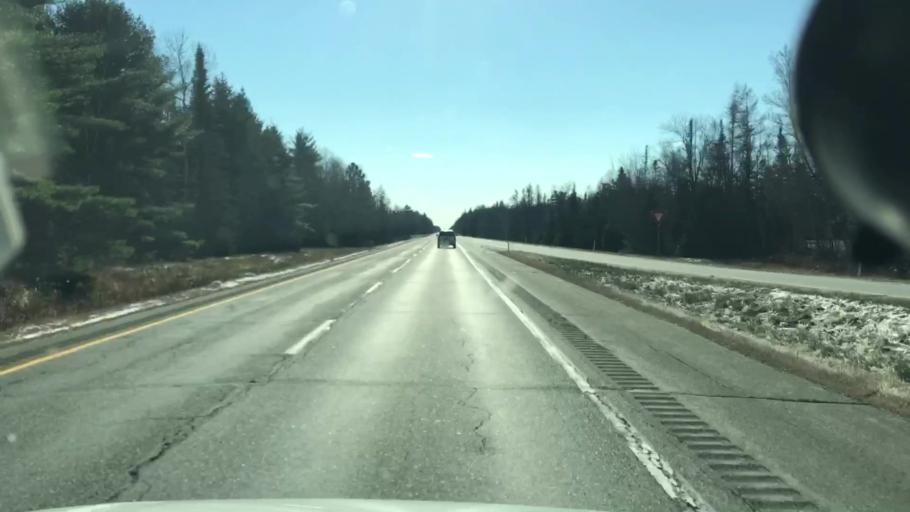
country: US
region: Maine
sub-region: Penobscot County
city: Milford
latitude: 44.9937
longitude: -68.7029
